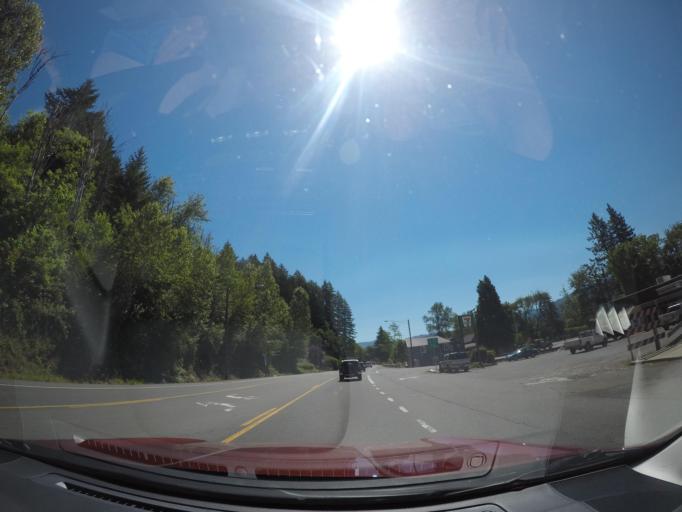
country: US
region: Oregon
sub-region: Linn County
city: Mill City
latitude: 44.7569
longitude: -122.4793
